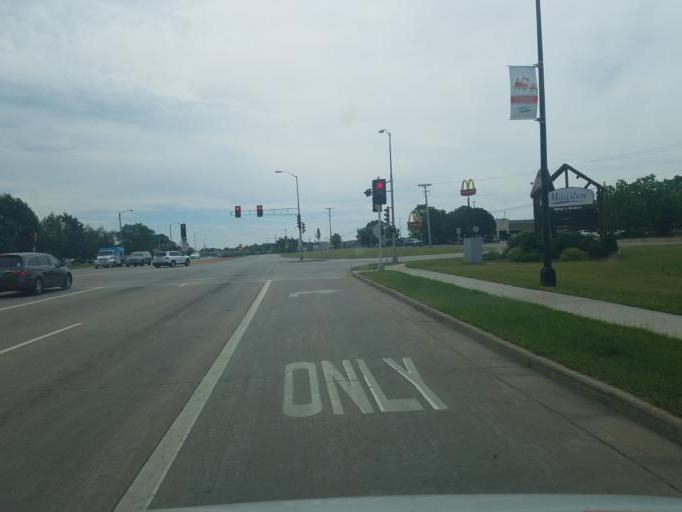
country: US
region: Wisconsin
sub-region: Juneau County
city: Mauston
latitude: 43.7969
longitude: -90.0636
